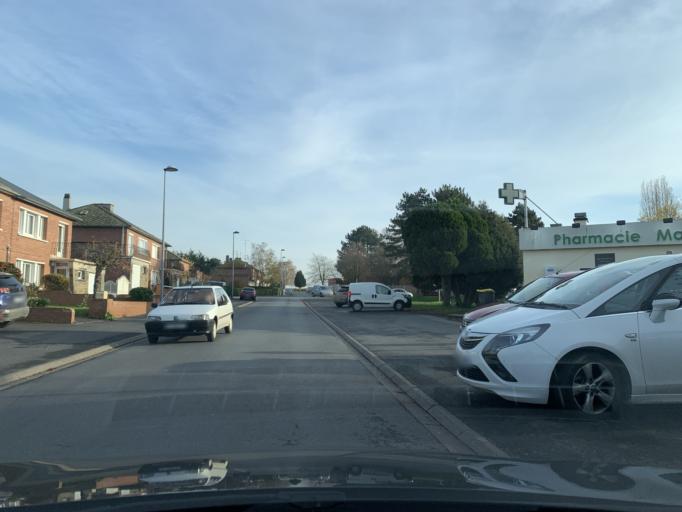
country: FR
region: Nord-Pas-de-Calais
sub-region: Departement du Nord
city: Cambrai
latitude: 50.1616
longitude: 3.2596
